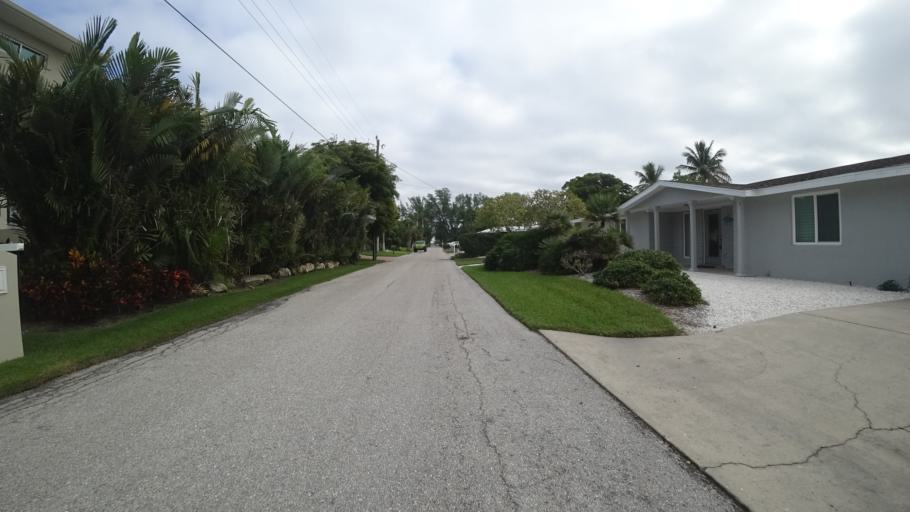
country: US
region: Florida
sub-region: Manatee County
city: Longboat Key
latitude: 27.4174
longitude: -82.6580
